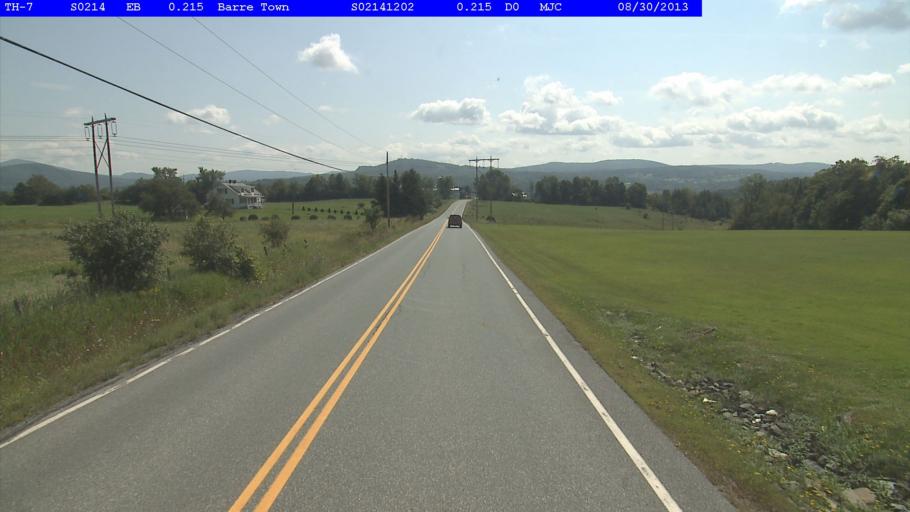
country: US
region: Vermont
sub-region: Washington County
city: South Barre
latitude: 44.1871
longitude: -72.5219
